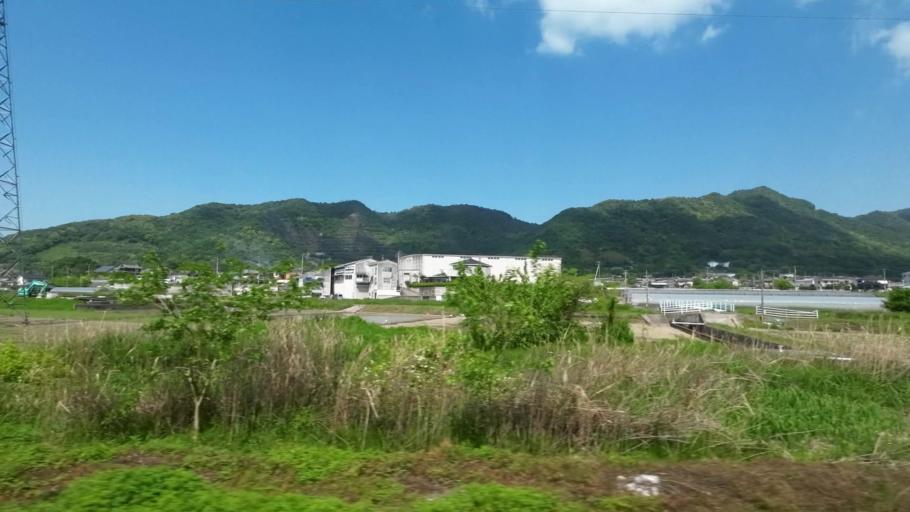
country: JP
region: Kagawa
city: Kan'onjicho
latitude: 34.1478
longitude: 133.6866
